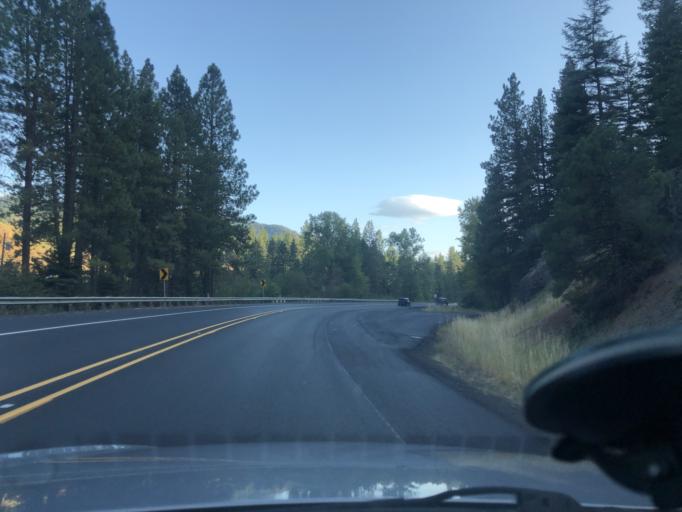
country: US
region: Washington
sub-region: Kittitas County
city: Cle Elum
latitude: 47.2512
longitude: -120.6924
